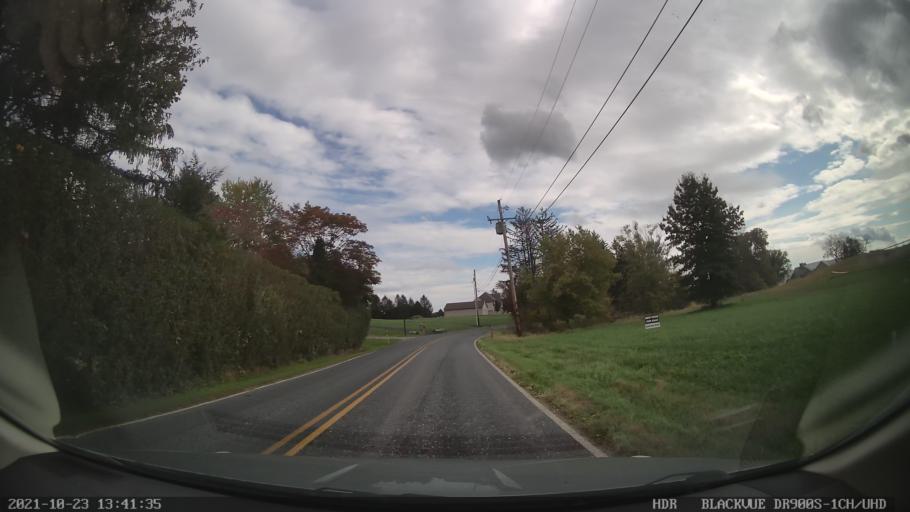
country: US
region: Pennsylvania
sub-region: Berks County
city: Bally
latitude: 40.4123
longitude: -75.5627
